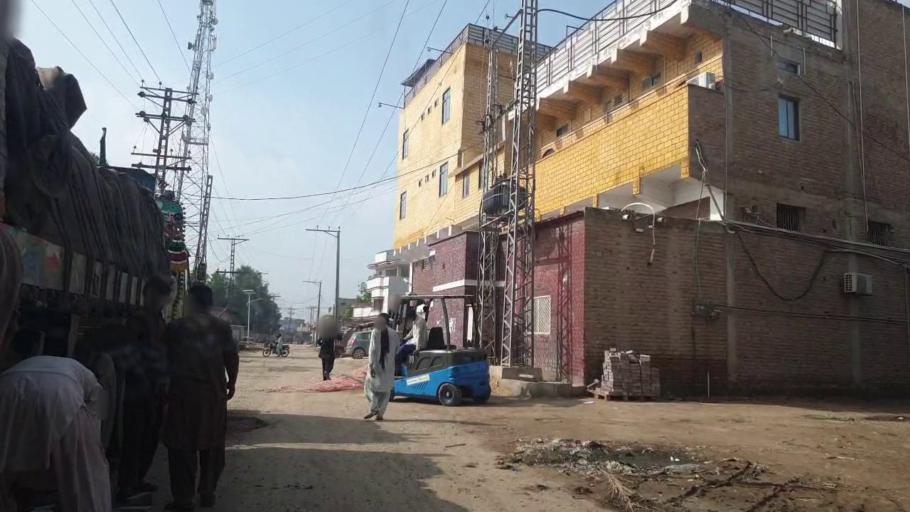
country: PK
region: Sindh
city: Khairpur
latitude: 27.5922
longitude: 68.7786
